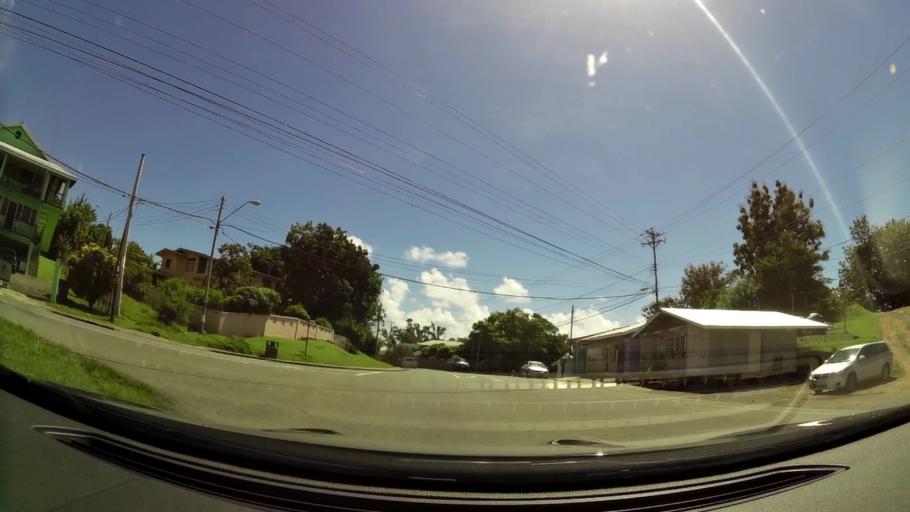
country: TT
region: Tobago
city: Scarborough
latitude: 11.1759
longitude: -60.7876
